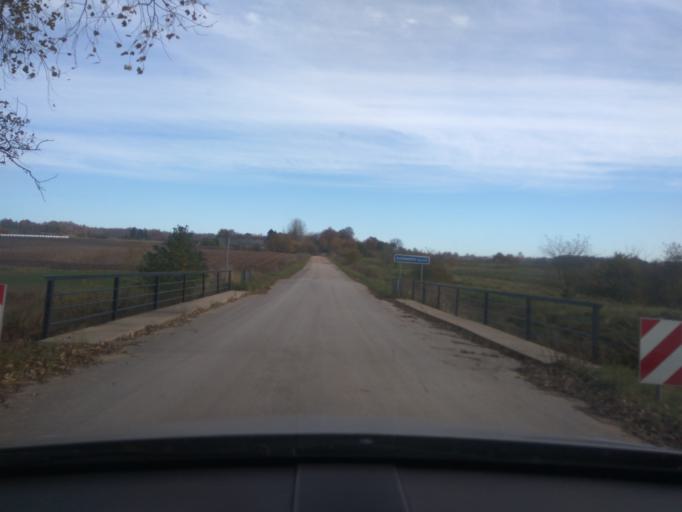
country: LV
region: Alsunga
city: Alsunga
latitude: 56.8692
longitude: 21.6877
